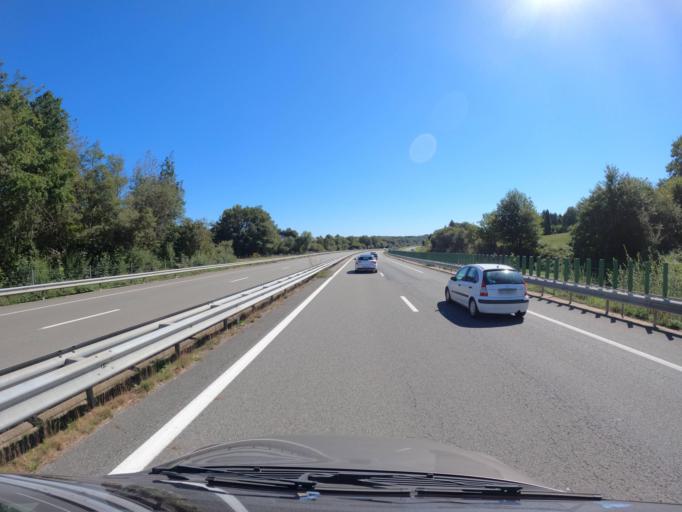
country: FR
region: Limousin
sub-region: Departement de la Creuse
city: Saint-Vaury
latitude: 46.2095
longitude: 1.7478
